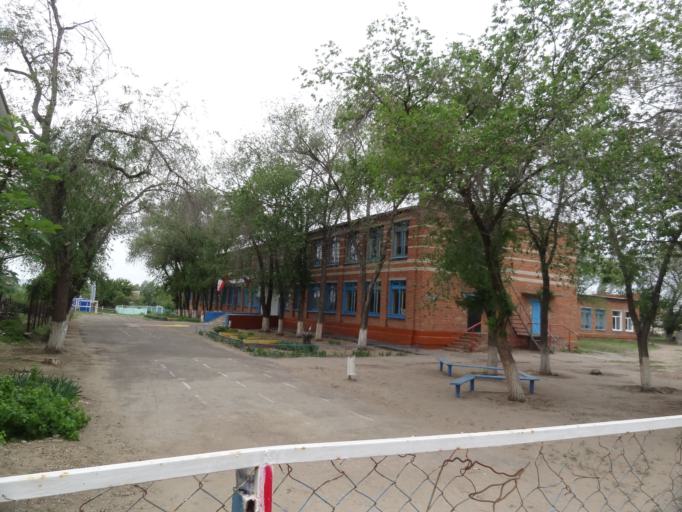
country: RU
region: Saratov
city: Privolzhskiy
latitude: 51.1848
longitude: 45.9177
